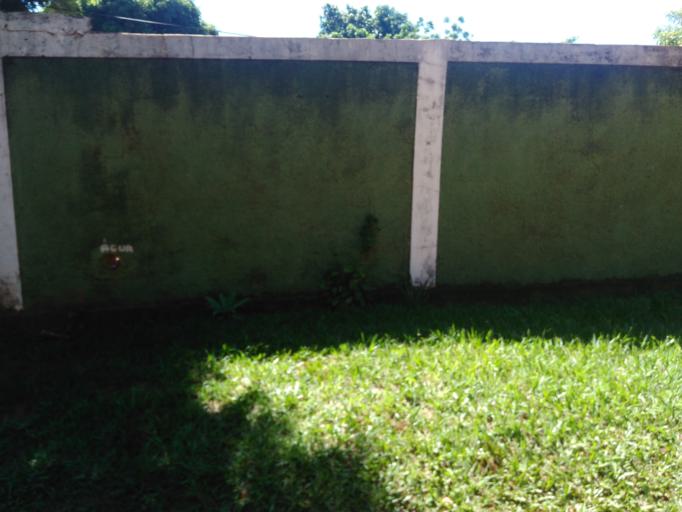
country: BR
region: Mato Grosso do Sul
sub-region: Ponta Pora
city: Ponta Pora
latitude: -22.5025
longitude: -55.7324
